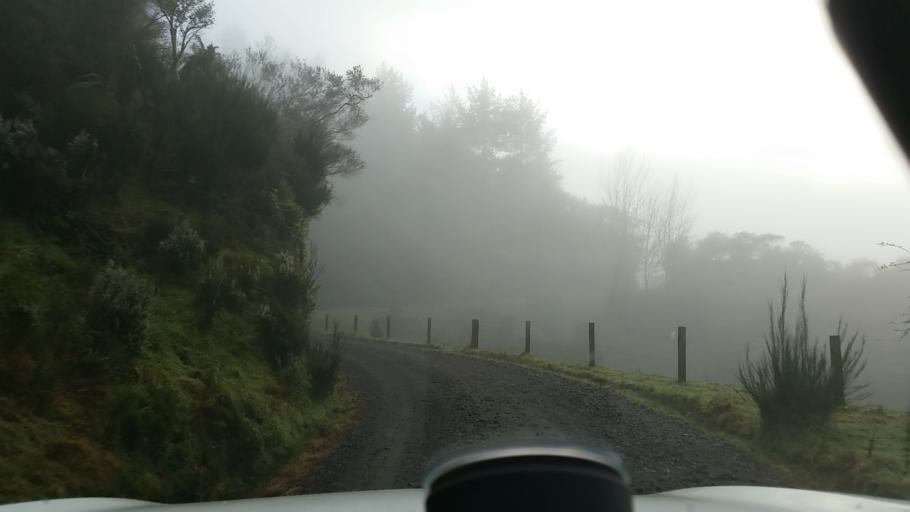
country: NZ
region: Taranaki
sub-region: South Taranaki District
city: Eltham
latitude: -39.4134
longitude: 174.4297
